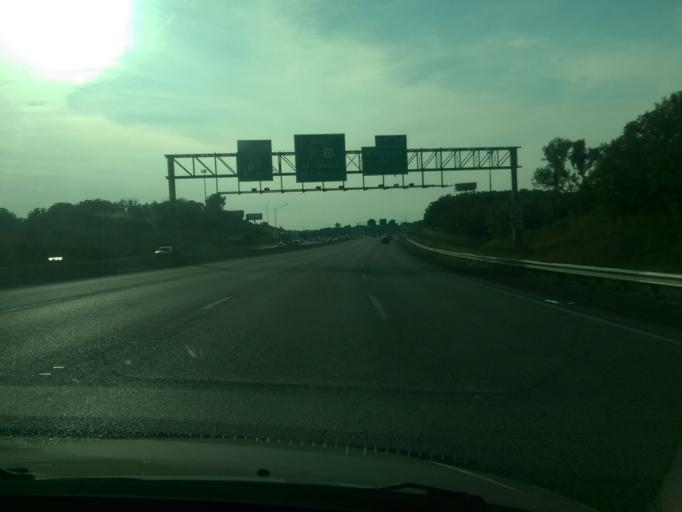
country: US
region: Missouri
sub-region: Platte County
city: Riverside
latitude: 39.1859
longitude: -94.5978
